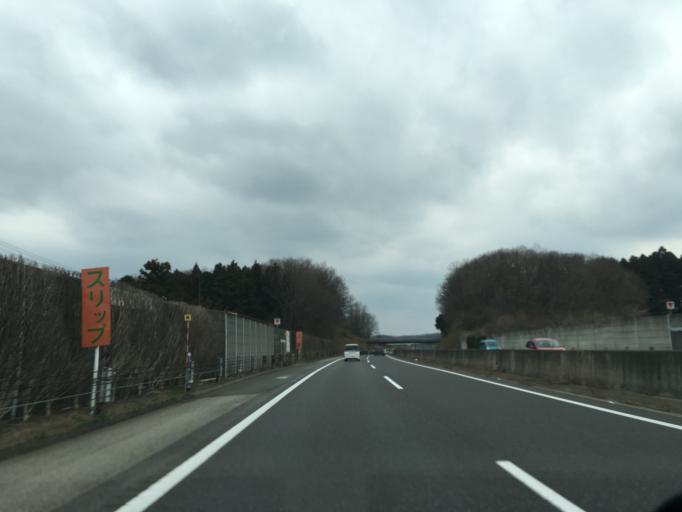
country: JP
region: Fukushima
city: Sukagawa
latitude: 37.2311
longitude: 140.3251
